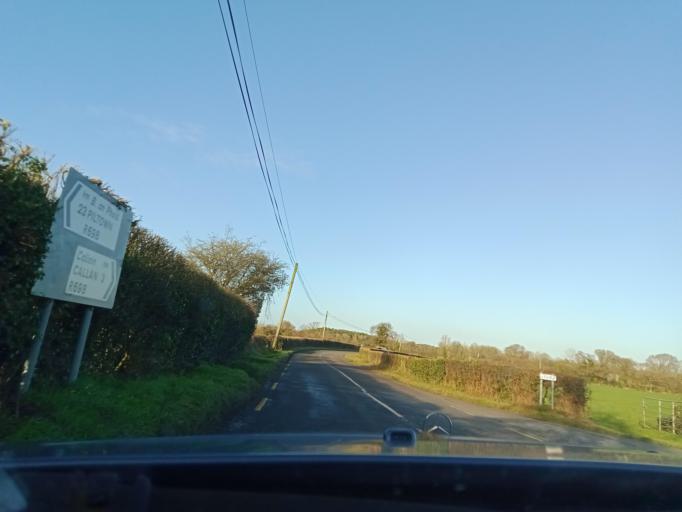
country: IE
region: Leinster
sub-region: Kilkenny
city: Callan
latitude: 52.5152
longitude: -7.3858
